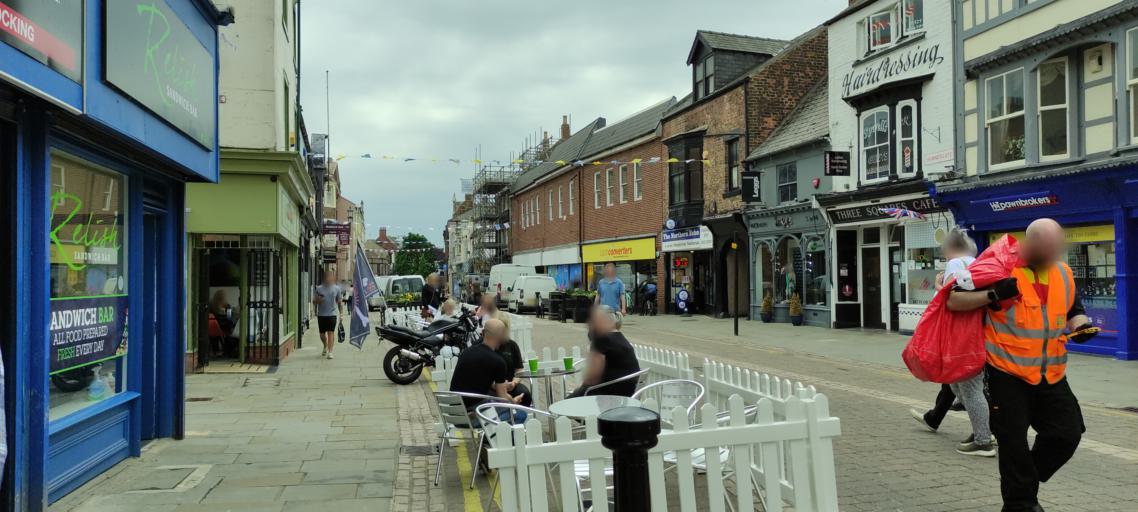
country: GB
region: England
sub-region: Darlington
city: Darlington
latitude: 54.5251
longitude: -1.5575
